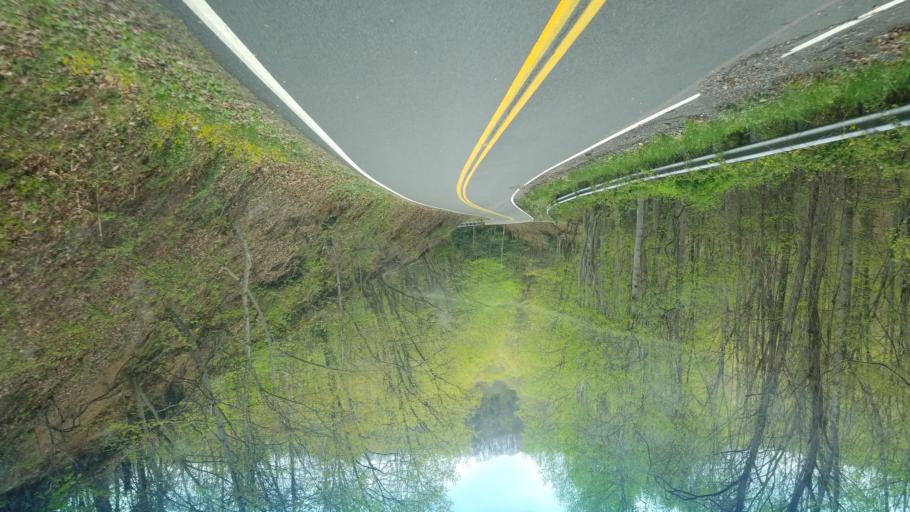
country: US
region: Virginia
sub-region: Tazewell County
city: Tazewell
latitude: 37.0078
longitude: -81.5167
